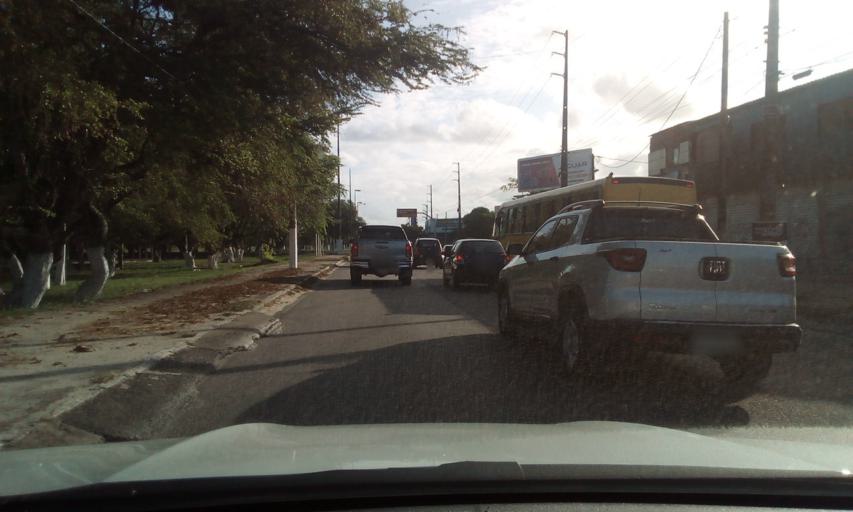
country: BR
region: Pernambuco
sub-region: Olinda
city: Olinda
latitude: -8.0293
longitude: -34.8662
